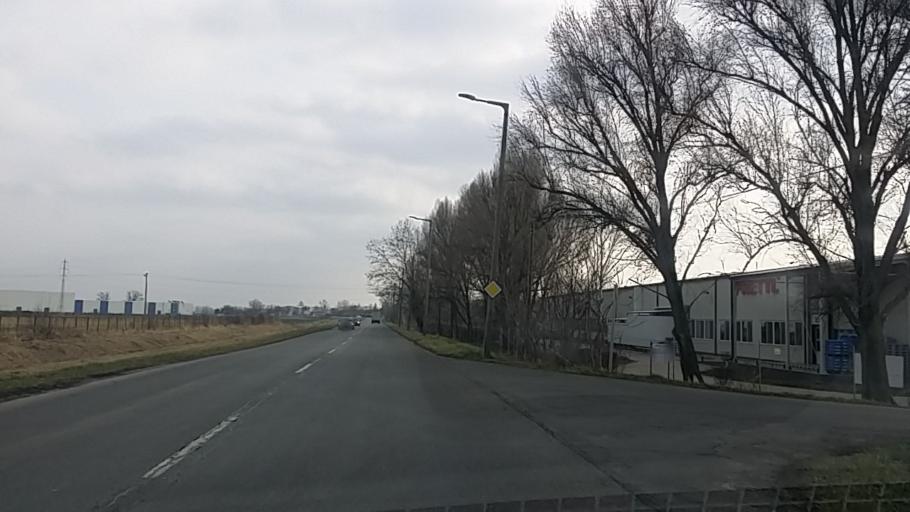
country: HU
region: Tolna
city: Szekszard
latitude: 46.3494
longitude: 18.7238
